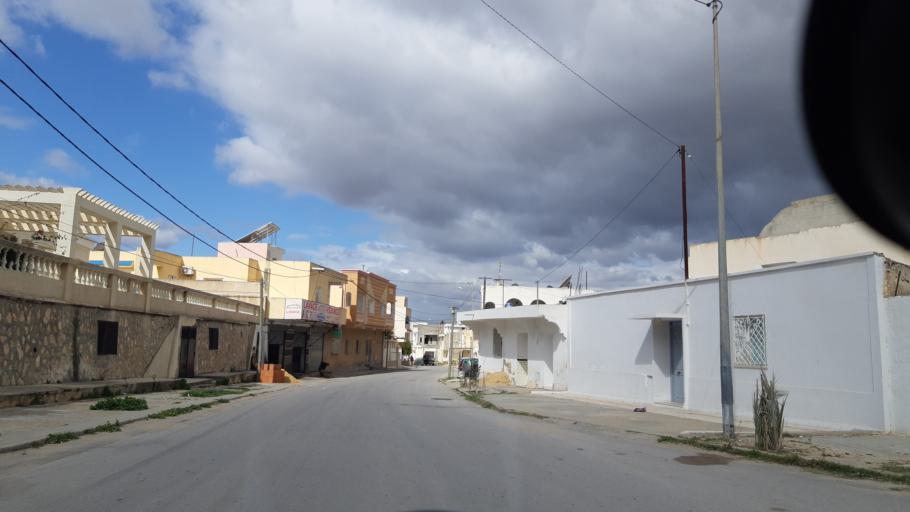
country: TN
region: Susah
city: Akouda
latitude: 35.8721
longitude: 10.5240
